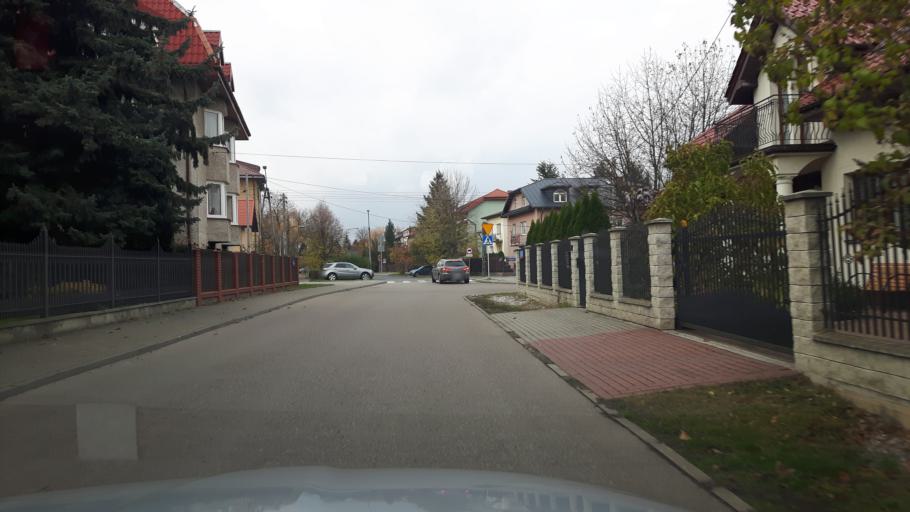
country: PL
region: Masovian Voivodeship
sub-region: Warszawa
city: Targowek
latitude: 52.2886
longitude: 21.0666
